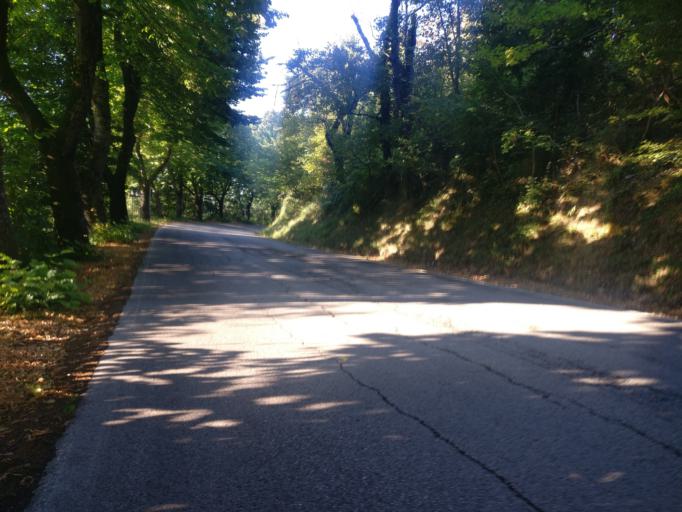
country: IT
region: The Marches
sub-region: Provincia di Ascoli Piceno
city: Montedinove
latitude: 42.9793
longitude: 13.5960
